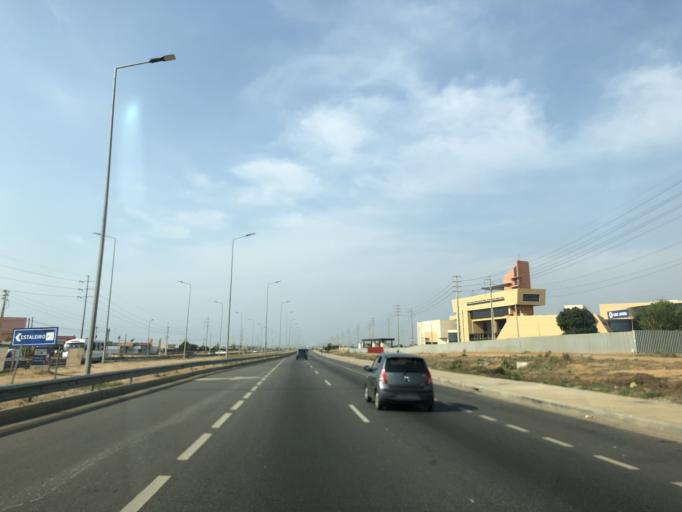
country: AO
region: Luanda
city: Luanda
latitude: -8.9646
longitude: 13.2561
